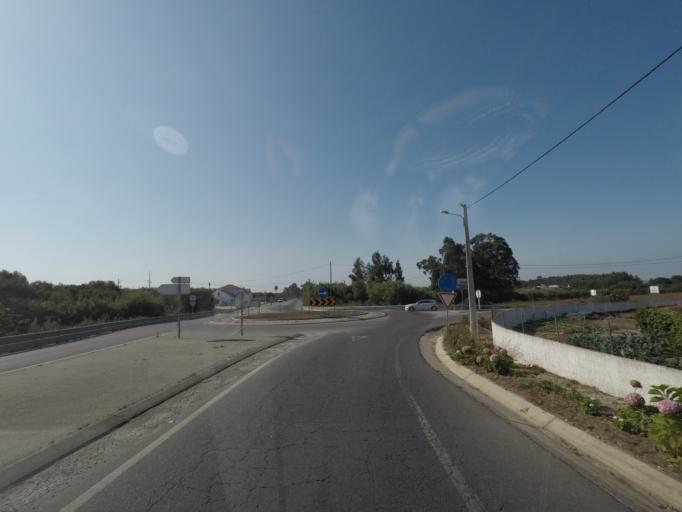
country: PT
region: Beja
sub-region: Odemira
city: Vila Nova de Milfontes
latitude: 37.6564
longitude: -8.7546
